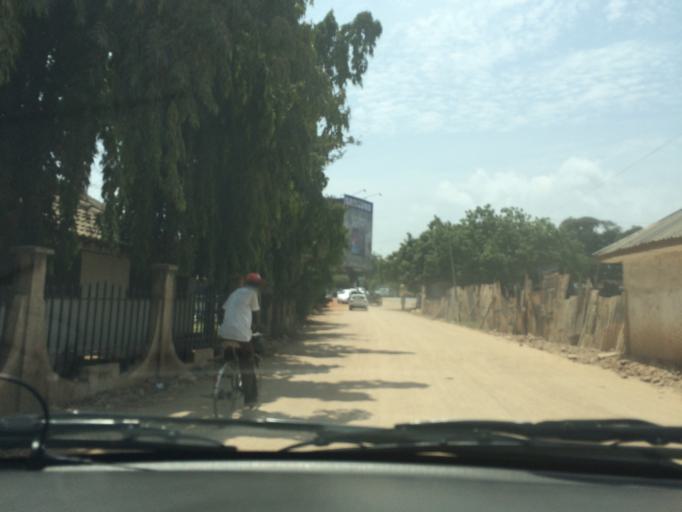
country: TZ
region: Dar es Salaam
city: Magomeni
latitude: -6.7705
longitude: 39.2649
